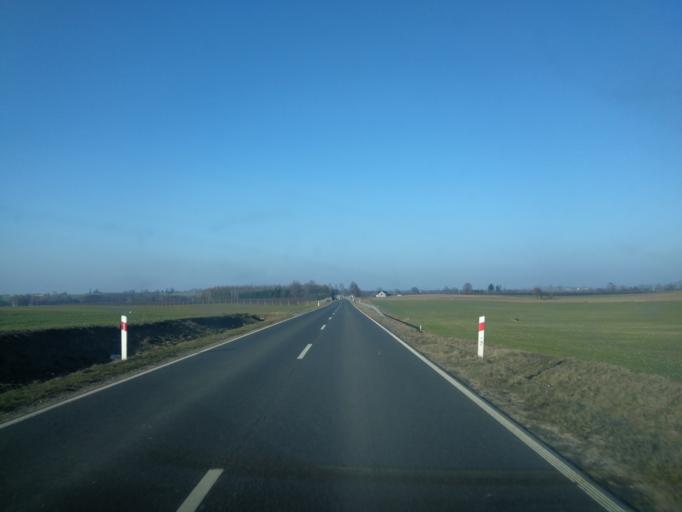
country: PL
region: Warmian-Masurian Voivodeship
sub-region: Powiat ilawski
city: Lubawa
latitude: 53.4443
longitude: 19.7771
